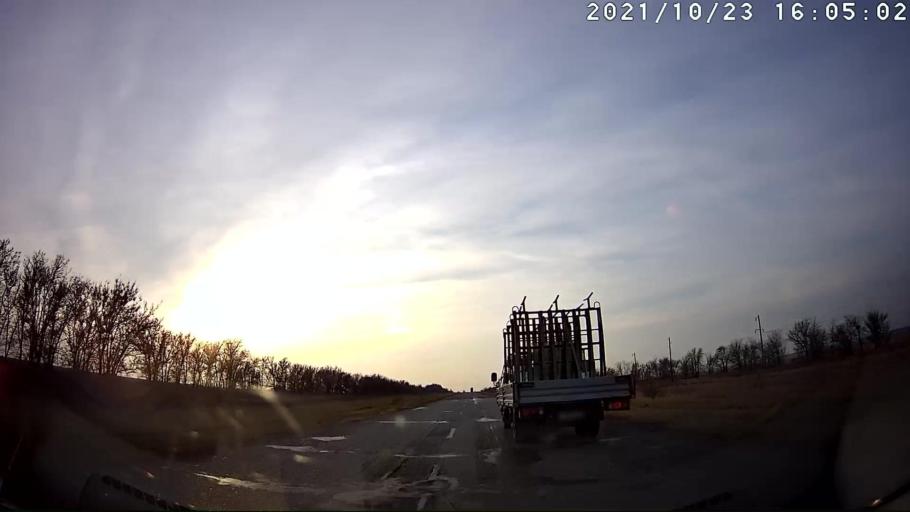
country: RU
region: Volgograd
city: Kotel'nikovo
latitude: 47.9286
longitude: 43.7902
